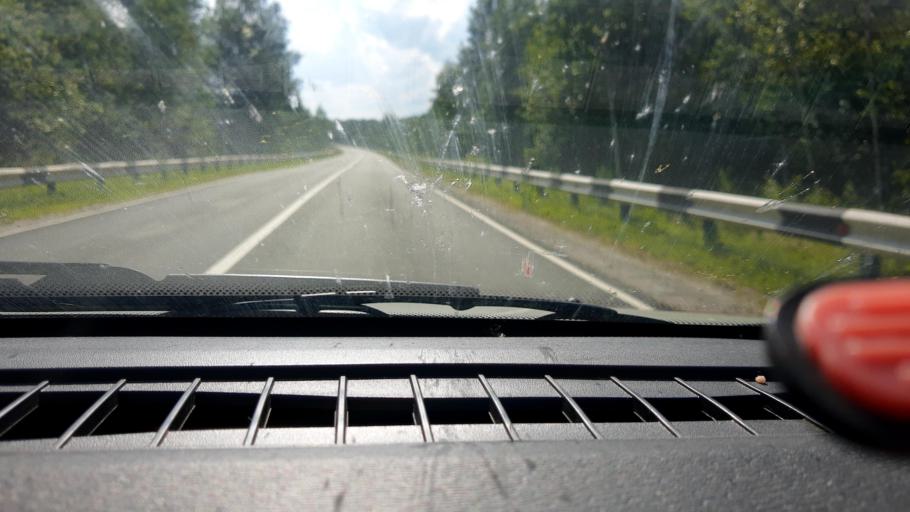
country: RU
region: Nizjnij Novgorod
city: Krasnyye Baki
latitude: 57.1130
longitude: 45.2001
